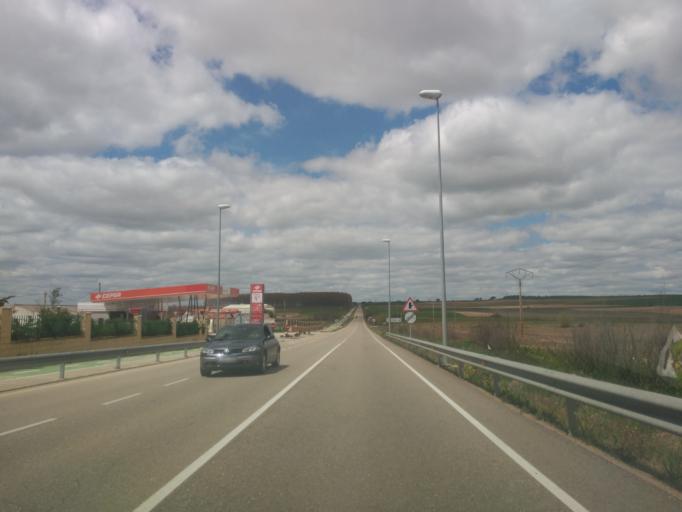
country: ES
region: Castille and Leon
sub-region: Provincia de Salamanca
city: Villamayor
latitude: 41.0180
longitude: -5.7164
